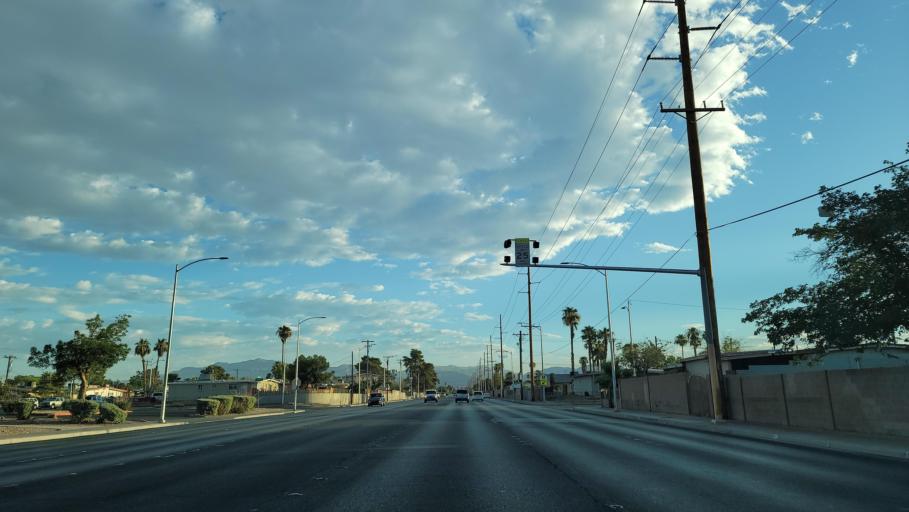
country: US
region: Nevada
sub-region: Clark County
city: North Las Vegas
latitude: 36.1833
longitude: -115.0983
